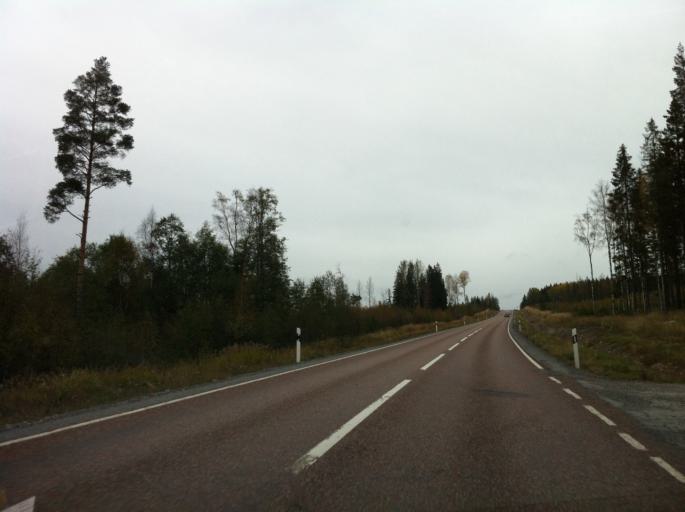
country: SE
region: Dalarna
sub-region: Ludvika Kommun
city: Grangesberg
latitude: 60.0087
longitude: 14.9928
